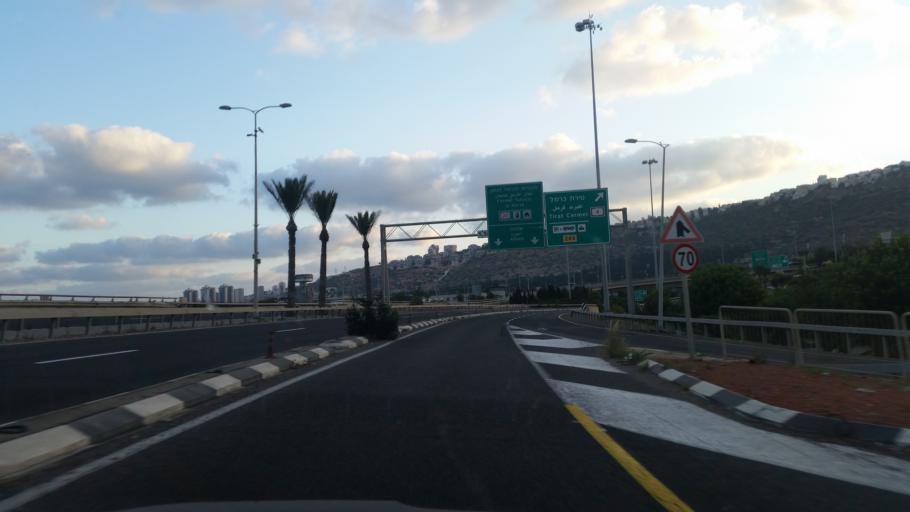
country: IL
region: Haifa
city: Tirat Karmel
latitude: 32.7908
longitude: 34.9574
